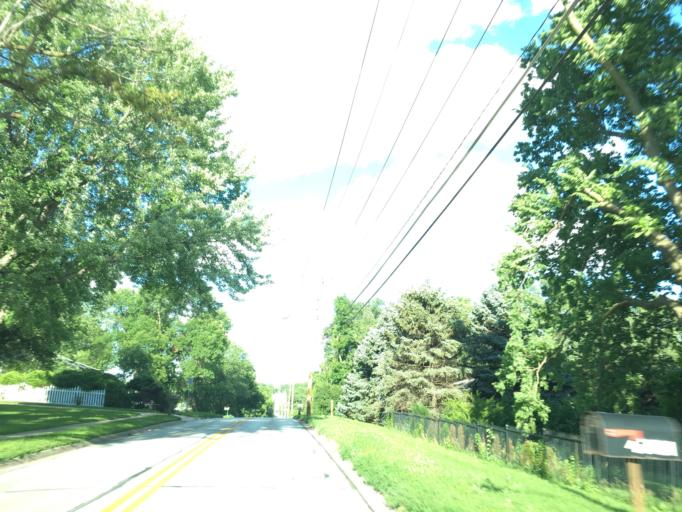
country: US
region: Nebraska
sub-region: Sarpy County
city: La Vista
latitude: 41.1908
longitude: -95.9844
